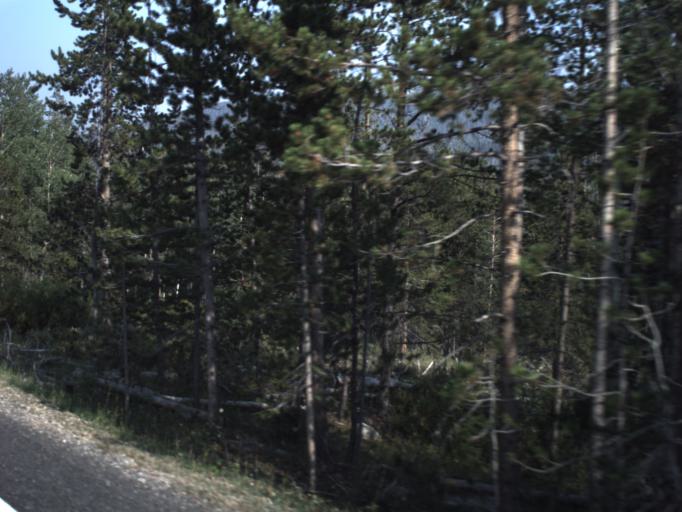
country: US
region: Wyoming
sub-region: Uinta County
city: Evanston
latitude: 40.8271
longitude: -110.8599
